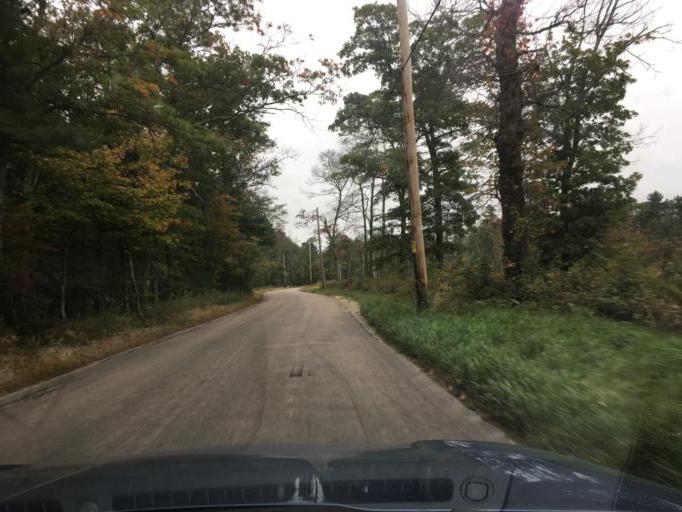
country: US
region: Rhode Island
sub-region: Washington County
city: Exeter
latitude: 41.5933
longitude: -71.5637
